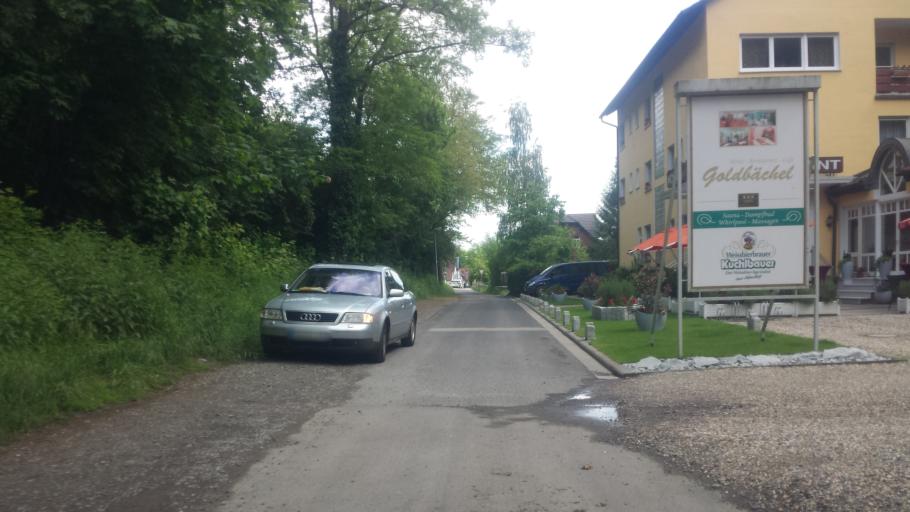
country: DE
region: Rheinland-Pfalz
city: Wachenheim
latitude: 49.4355
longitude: 8.1670
